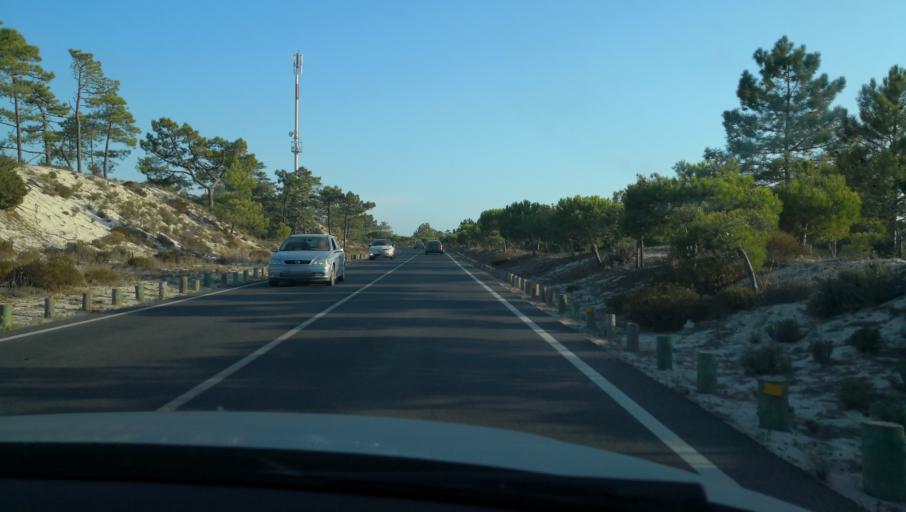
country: PT
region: Setubal
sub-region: Setubal
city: Setubal
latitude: 38.4717
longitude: -8.8845
